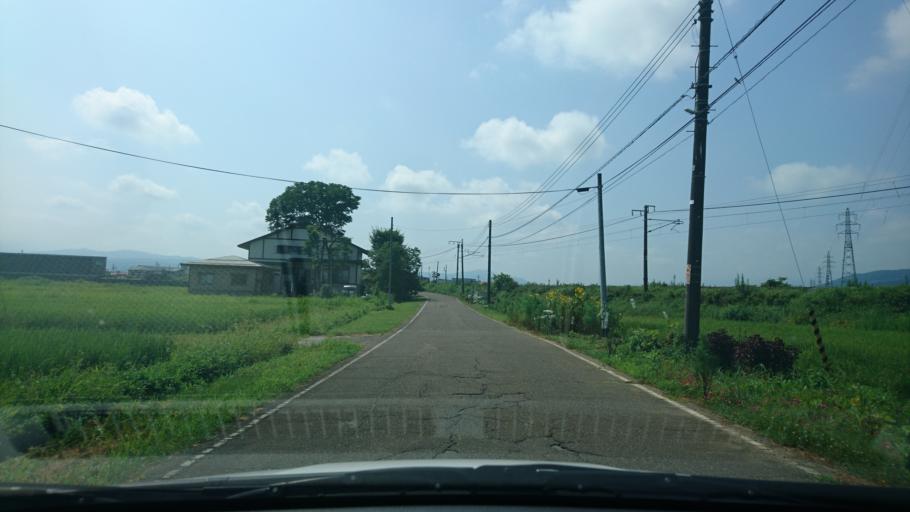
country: JP
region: Niigata
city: Arai
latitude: 37.0696
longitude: 138.2554
